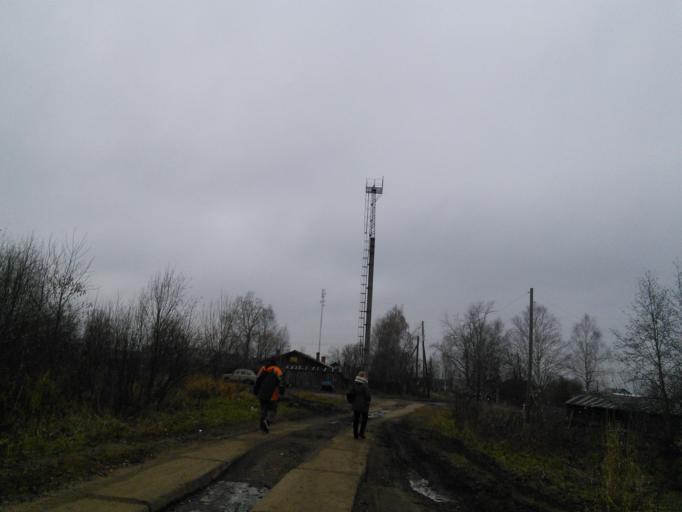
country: RU
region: Vologda
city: Kharovsk
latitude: 59.8077
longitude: 40.1760
